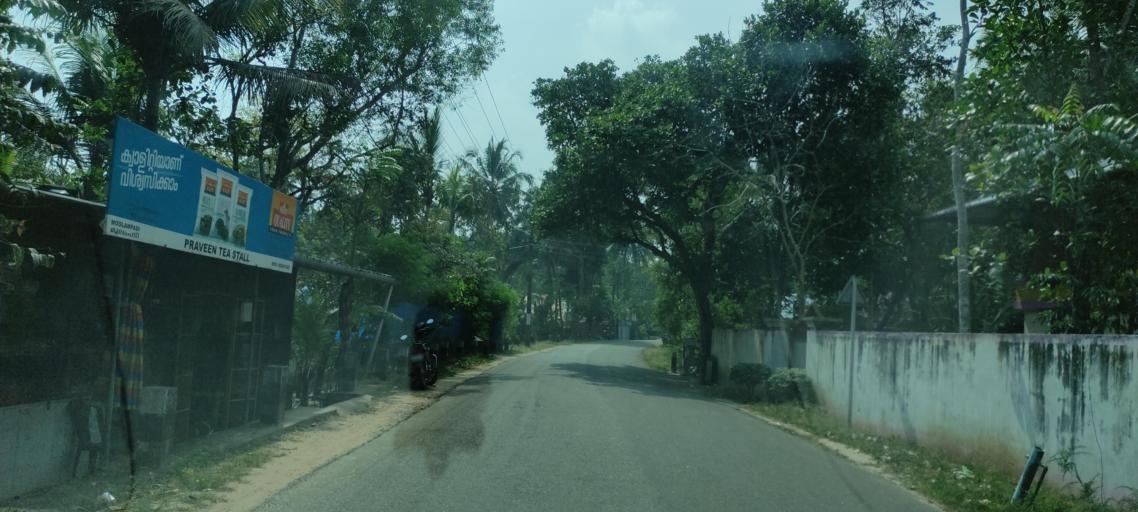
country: IN
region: Kerala
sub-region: Alappuzha
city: Shertallai
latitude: 9.6349
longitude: 76.3530
